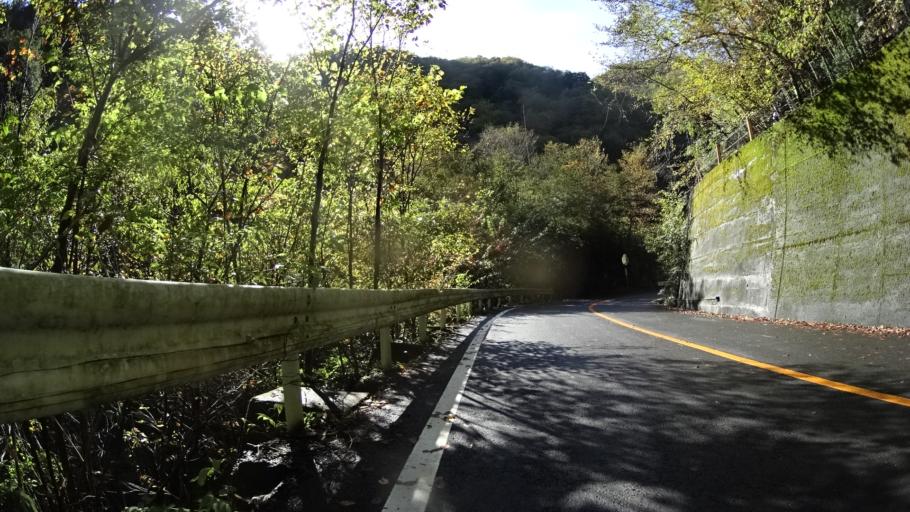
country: JP
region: Yamanashi
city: Enzan
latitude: 35.8029
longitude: 138.8524
